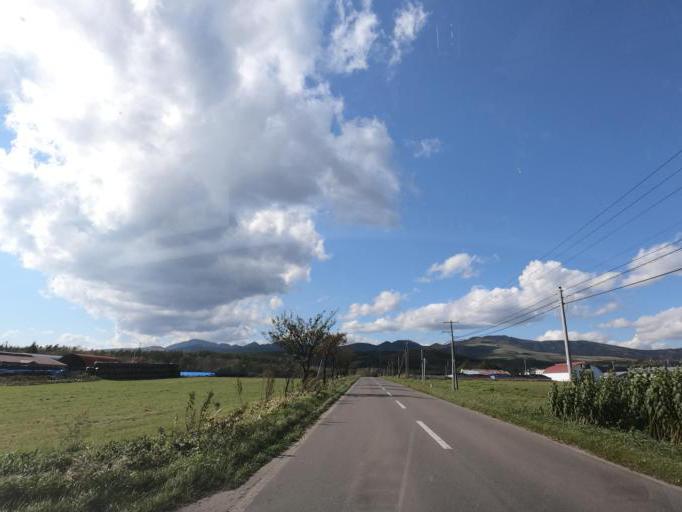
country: JP
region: Hokkaido
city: Otofuke
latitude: 43.2586
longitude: 143.2475
